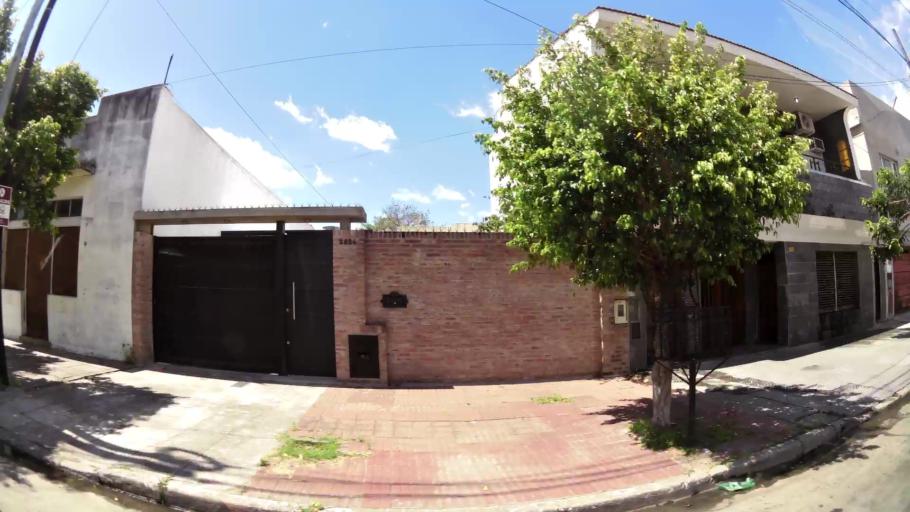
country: AR
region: Buenos Aires
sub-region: Partido de Lanus
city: Lanus
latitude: -34.6975
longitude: -58.4138
